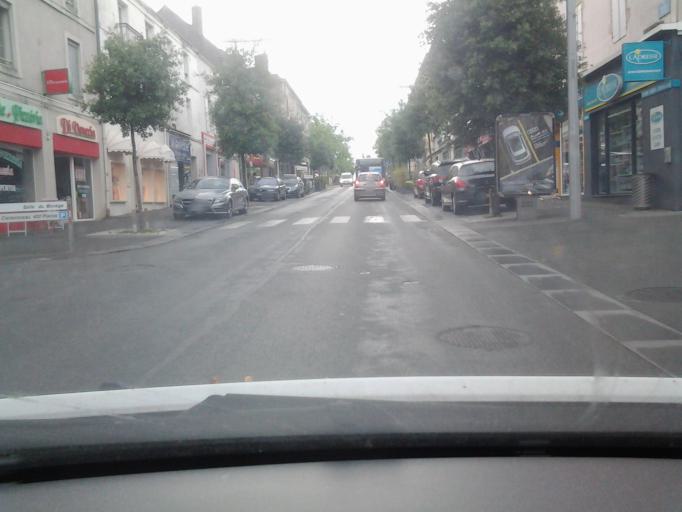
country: FR
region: Pays de la Loire
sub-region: Departement de la Vendee
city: La Roche-sur-Yon
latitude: 46.6691
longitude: -1.4259
